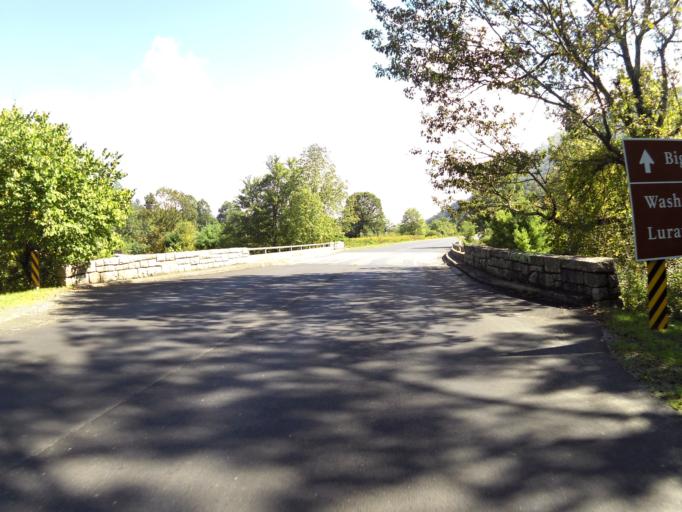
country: US
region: Virginia
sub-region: Page County
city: Luray
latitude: 38.6623
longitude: -78.3226
